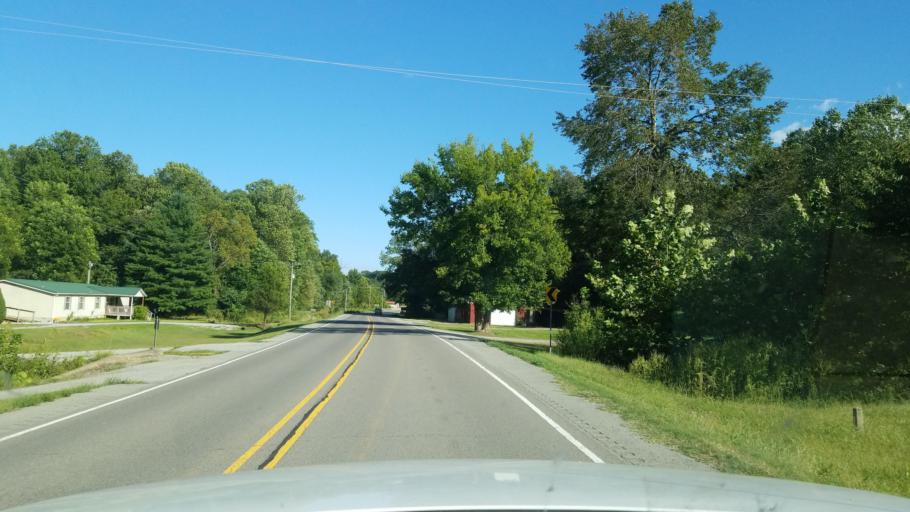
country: US
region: Illinois
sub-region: Hardin County
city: Rosiclare
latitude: 37.5820
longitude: -88.4399
